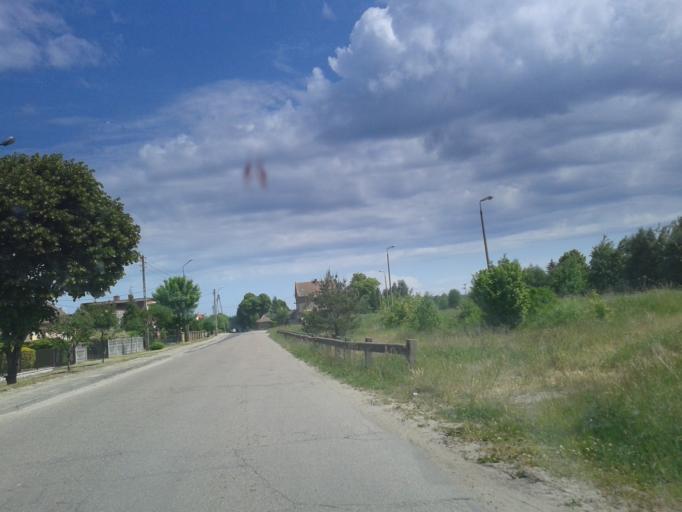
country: PL
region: Pomeranian Voivodeship
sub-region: Powiat koscierski
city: Karsin
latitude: 53.8958
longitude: 17.9283
